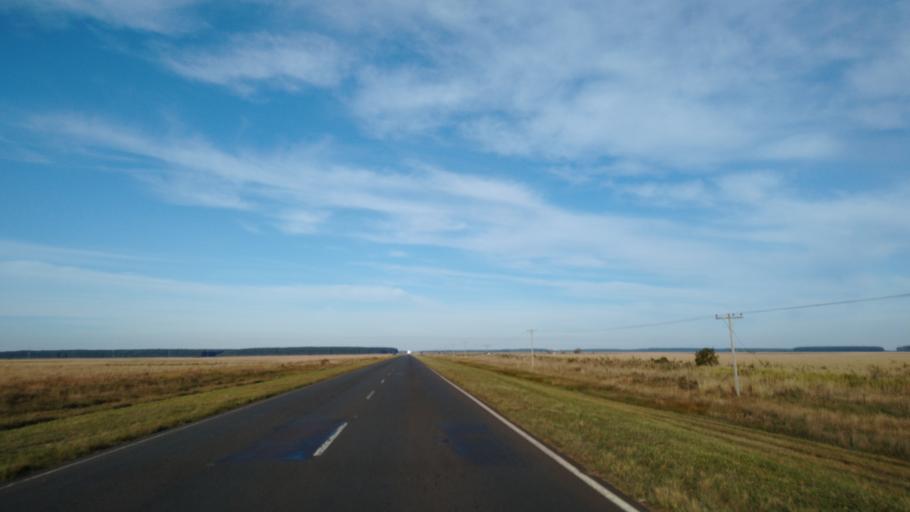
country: AR
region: Corrientes
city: La Cruz
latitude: -29.2879
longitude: -56.7657
